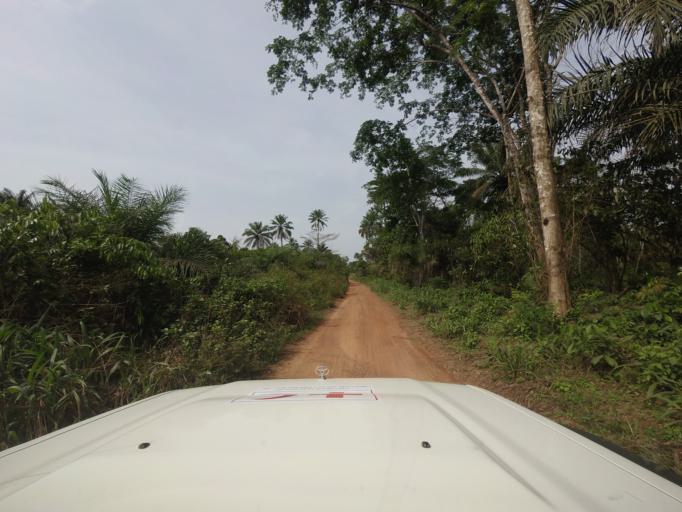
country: GN
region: Nzerekore
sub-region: Macenta
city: Macenta
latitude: 8.4931
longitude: -9.5362
